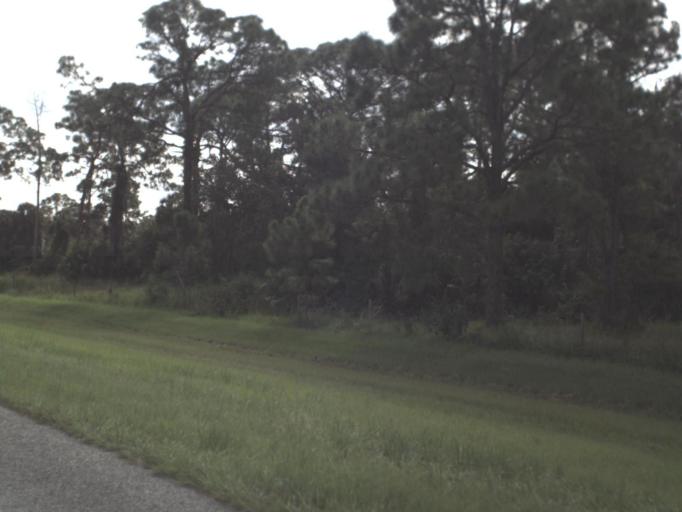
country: US
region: Florida
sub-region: Lee County
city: Alva
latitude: 26.7086
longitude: -81.6241
